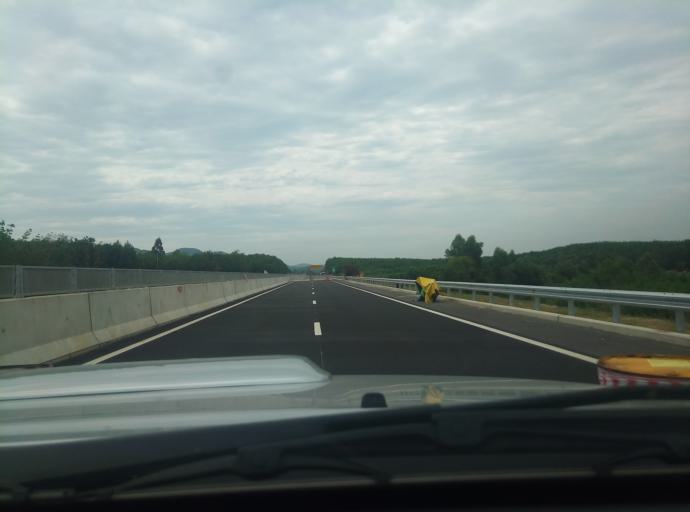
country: VN
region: Quang Nam
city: Nui Thanh
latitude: 15.4498
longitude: 108.5782
